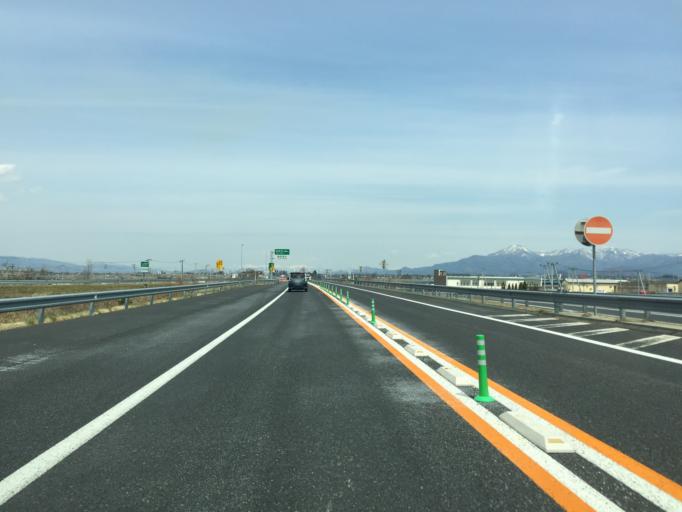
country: JP
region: Yamagata
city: Tendo
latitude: 38.3631
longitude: 140.3458
